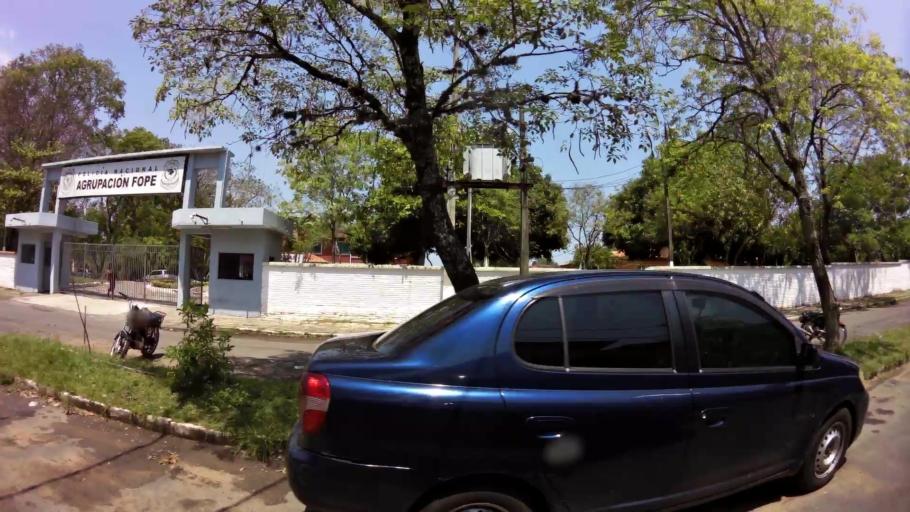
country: PY
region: Asuncion
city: Asuncion
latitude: -25.3063
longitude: -57.6501
